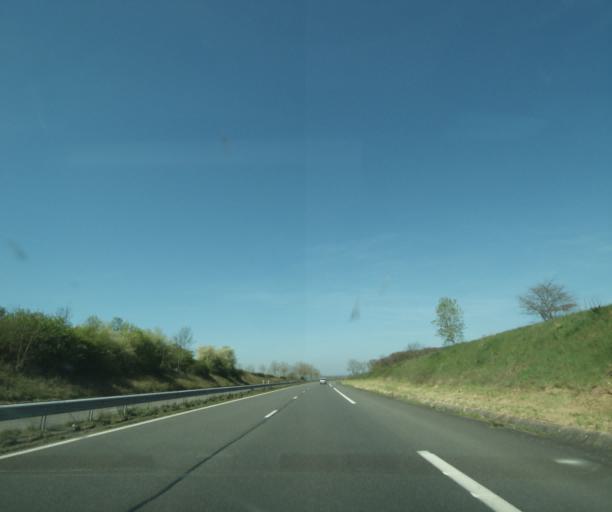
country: FR
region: Bourgogne
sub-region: Departement de la Nievre
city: Chaulgnes
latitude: 47.1168
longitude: 3.0606
